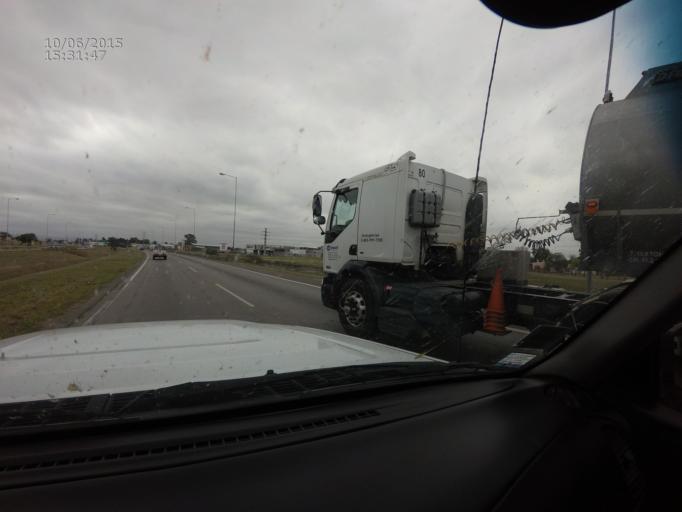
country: AR
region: Cordoba
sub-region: Departamento de Capital
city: Cordoba
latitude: -31.3655
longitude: -64.1326
